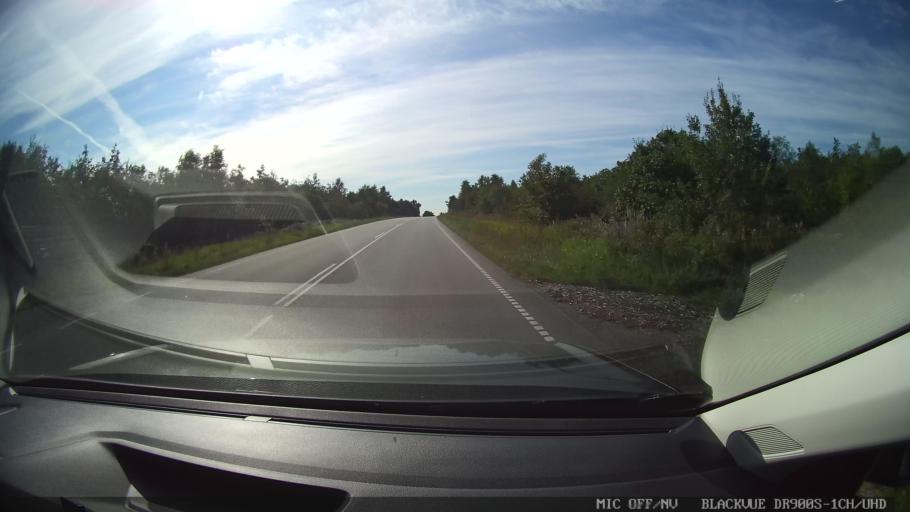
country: DK
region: North Denmark
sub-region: Mariagerfjord Kommune
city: Hadsund
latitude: 56.7541
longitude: 10.0714
